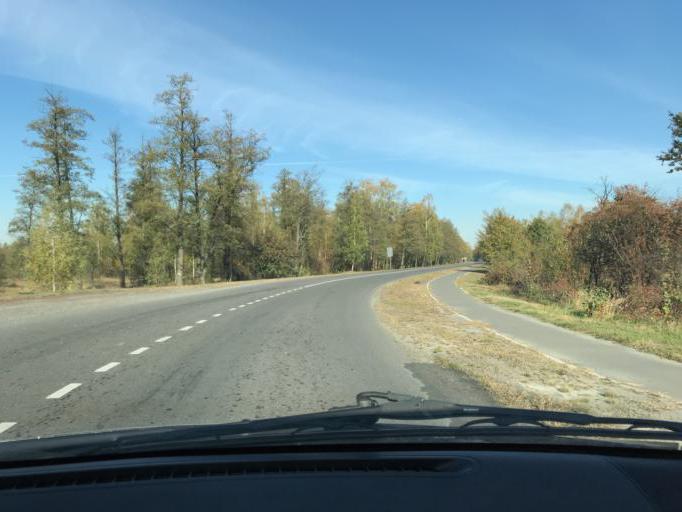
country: BY
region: Brest
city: Mikashevichy
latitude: 52.2325
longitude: 27.4497
